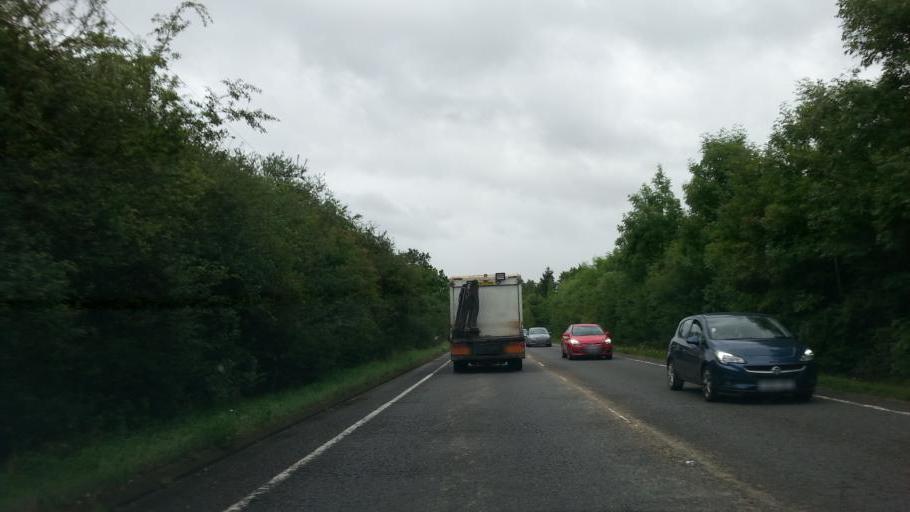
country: GB
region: England
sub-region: Northamptonshire
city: Oundle
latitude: 52.4608
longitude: -0.4620
